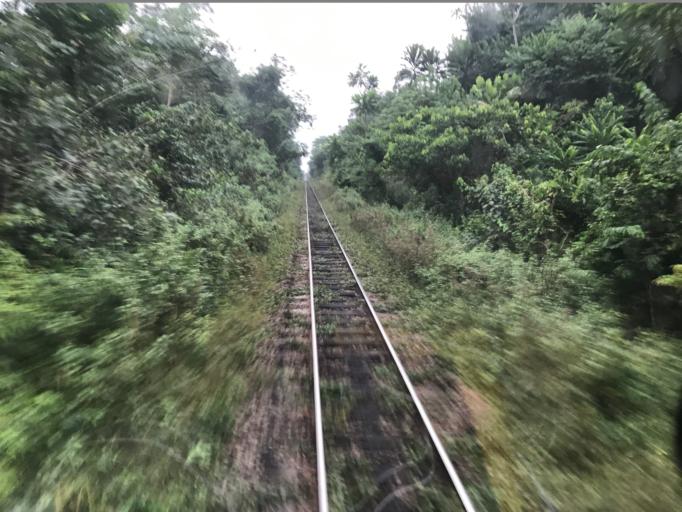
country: CM
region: Littoral
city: Edea
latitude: 3.9857
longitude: 10.0531
